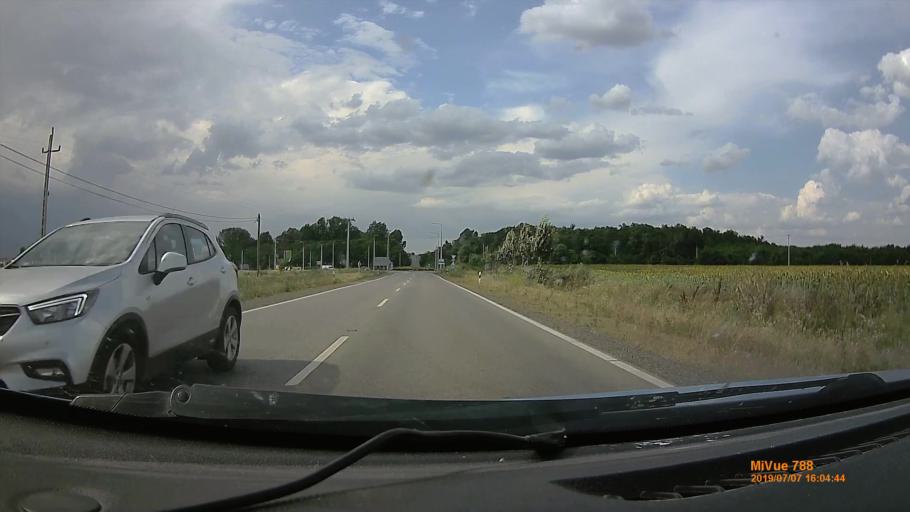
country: HU
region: Heves
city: Hatvan
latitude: 47.6569
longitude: 19.7244
